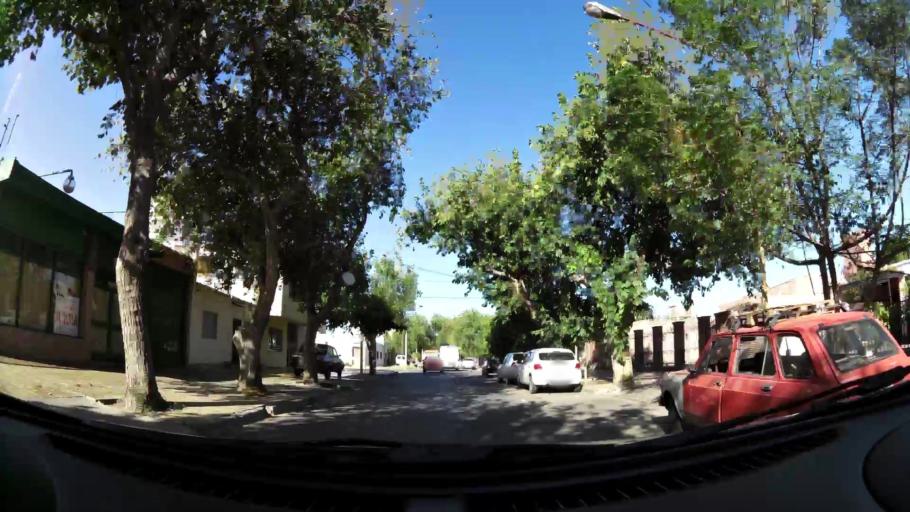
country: AR
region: San Juan
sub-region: Departamento de Santa Lucia
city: Santa Lucia
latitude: -31.5345
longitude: -68.5136
